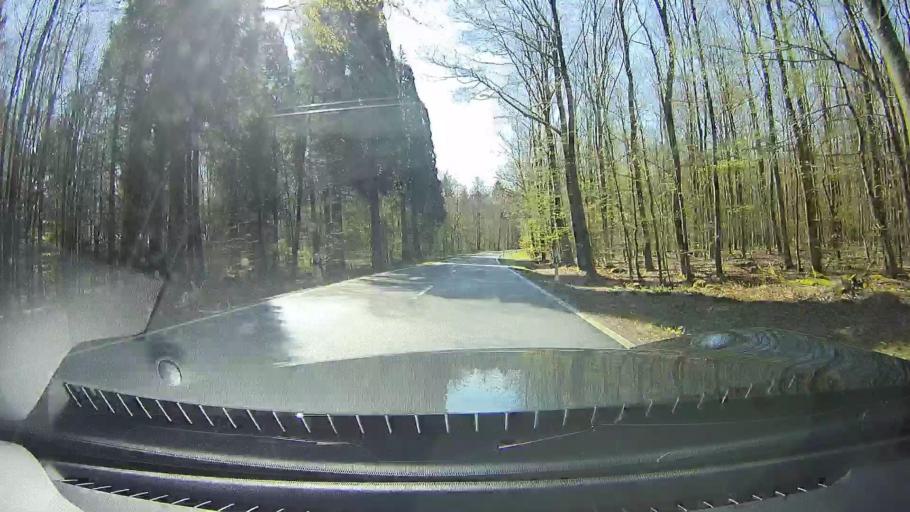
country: DE
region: Baden-Wuerttemberg
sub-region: Karlsruhe Region
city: Neunkirchen
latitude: 49.4162
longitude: 8.9833
